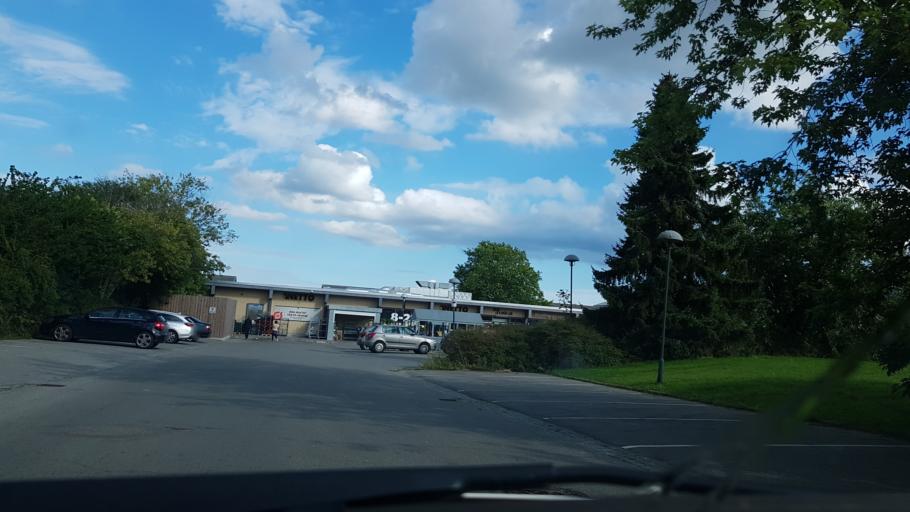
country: DK
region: Capital Region
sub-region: Fredensborg Kommune
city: Kokkedal
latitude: 55.9099
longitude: 12.4905
